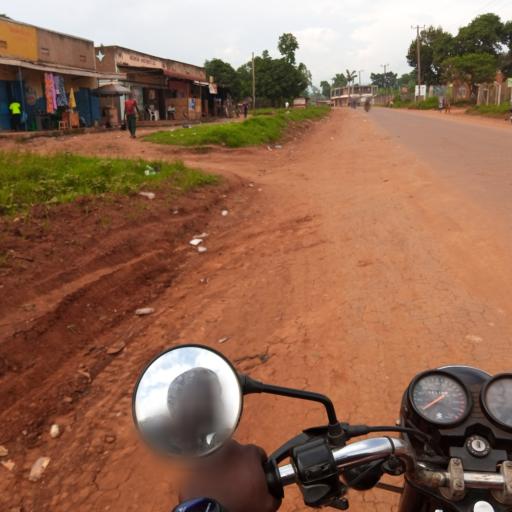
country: UG
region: Eastern Region
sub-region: Mbale District
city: Mbale
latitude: 1.0855
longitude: 34.1801
